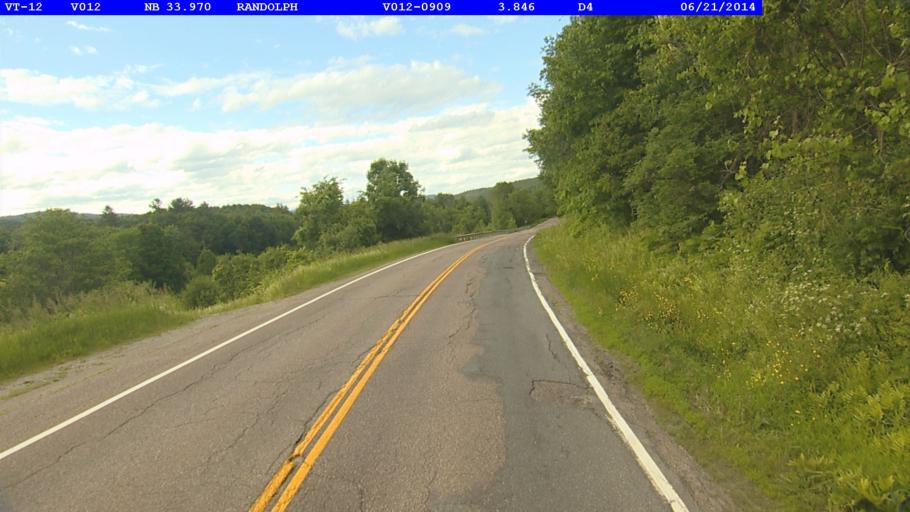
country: US
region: Vermont
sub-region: Orange County
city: Randolph
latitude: 43.9444
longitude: -72.6556
